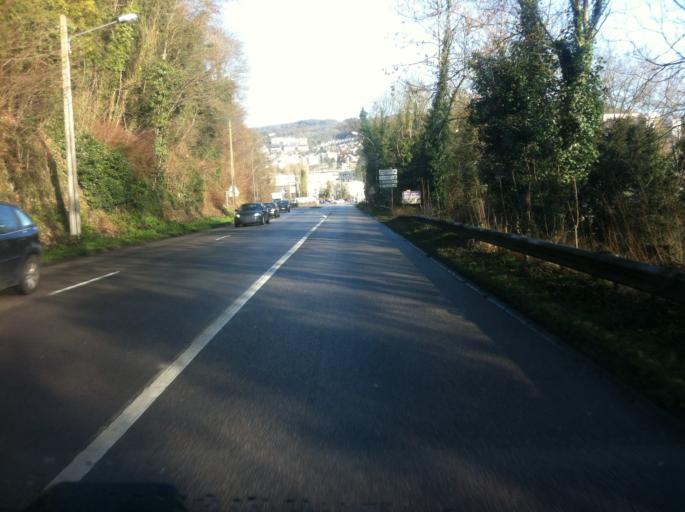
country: FR
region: Haute-Normandie
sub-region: Departement de la Seine-Maritime
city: Deville-les-Rouen
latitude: 49.4477
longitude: 1.0462
